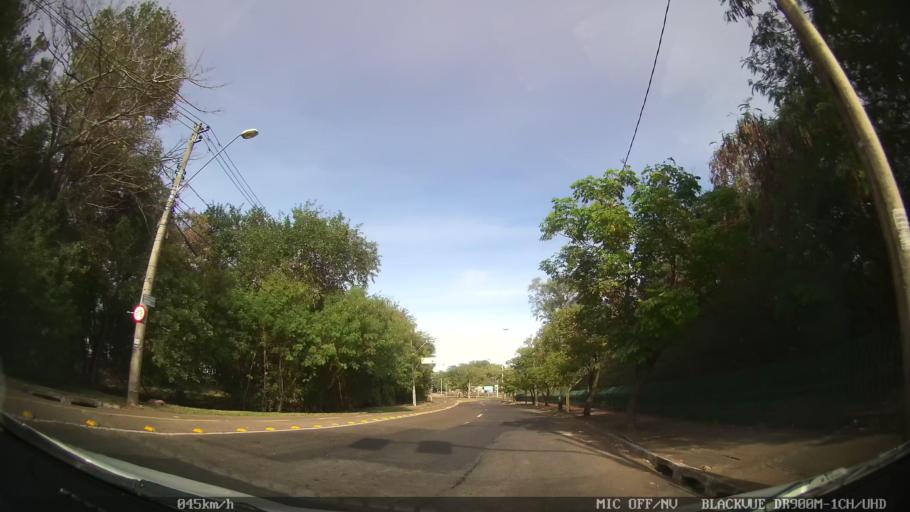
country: BR
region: Sao Paulo
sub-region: Piracicaba
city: Piracicaba
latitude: -22.7248
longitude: -47.6712
